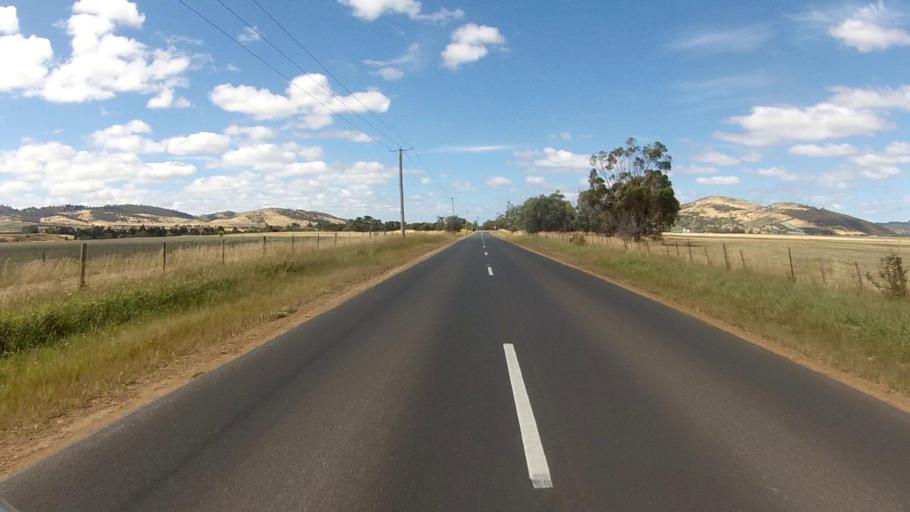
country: AU
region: Tasmania
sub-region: Clarence
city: Cambridge
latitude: -42.7214
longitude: 147.4343
